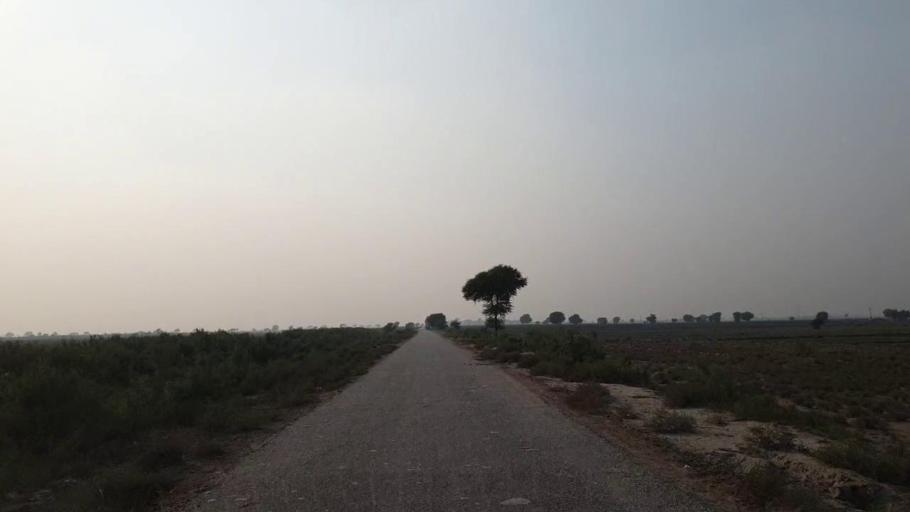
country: PK
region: Sindh
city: Bhan
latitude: 26.4887
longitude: 67.7223
